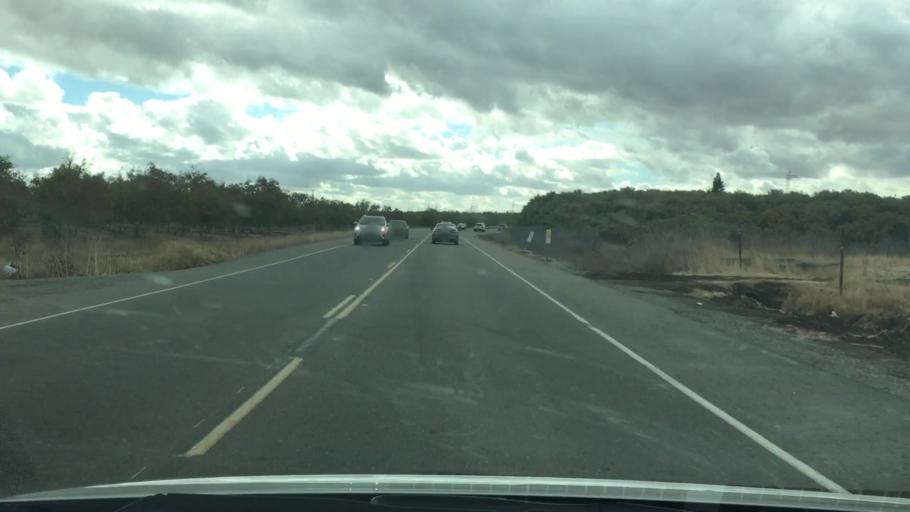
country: US
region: California
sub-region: Yolo County
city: Winters
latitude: 38.5522
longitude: -121.9028
